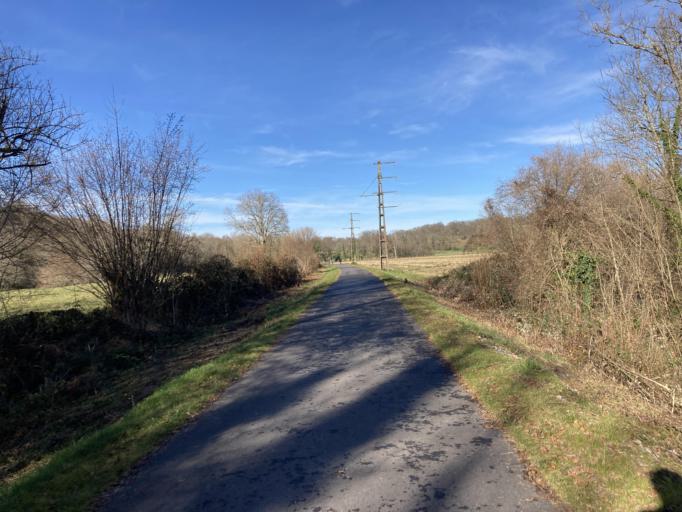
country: FR
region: Aquitaine
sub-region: Departement des Pyrenees-Atlantiques
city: Arudy
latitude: 43.1191
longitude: -0.4378
